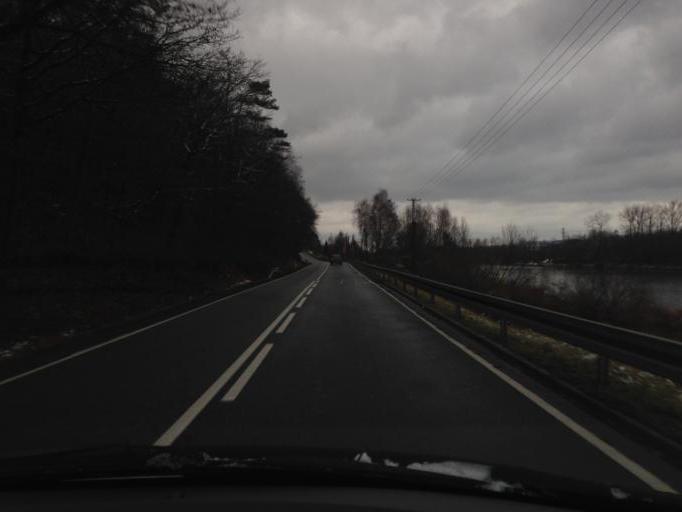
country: PL
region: Lesser Poland Voivodeship
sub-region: Powiat tarnowski
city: Zakliczyn
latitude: 49.8670
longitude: 20.7931
